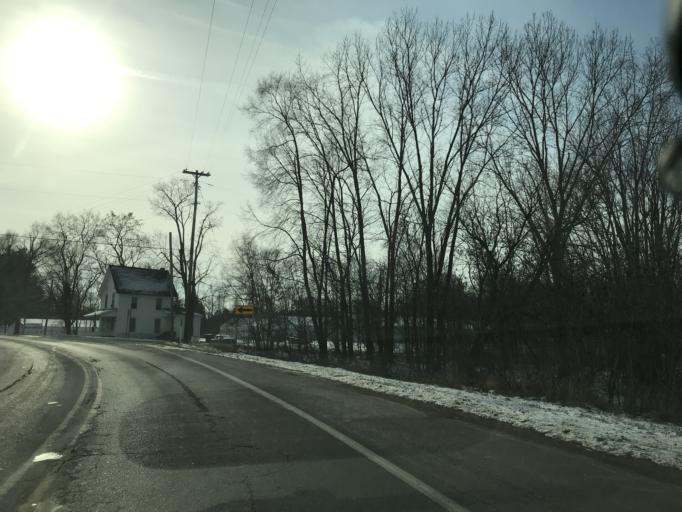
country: US
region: Michigan
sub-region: Barry County
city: Nashville
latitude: 42.5967
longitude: -85.0945
